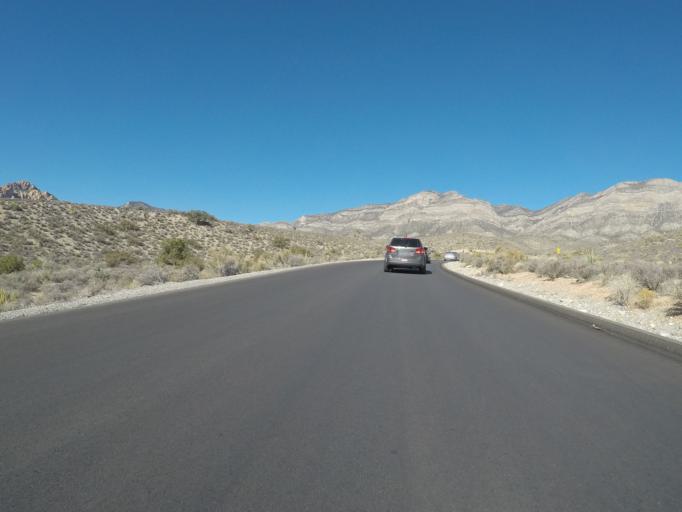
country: US
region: Nevada
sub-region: Clark County
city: Summerlin South
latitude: 36.1696
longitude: -115.4623
